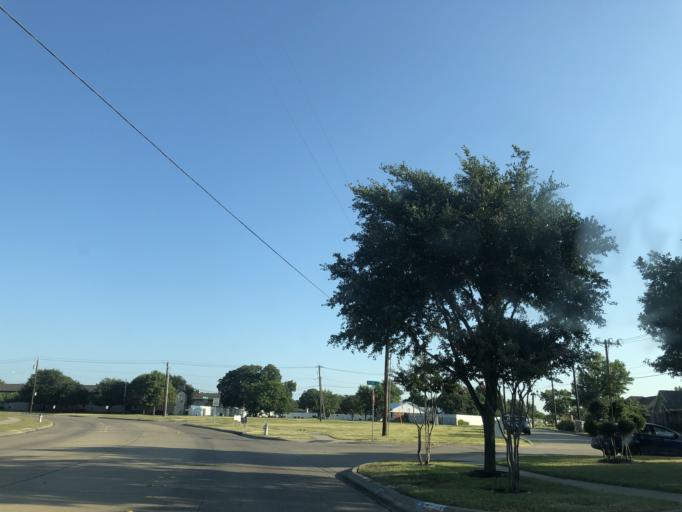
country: US
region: Texas
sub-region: Dallas County
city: Sunnyvale
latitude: 32.8473
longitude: -96.5606
